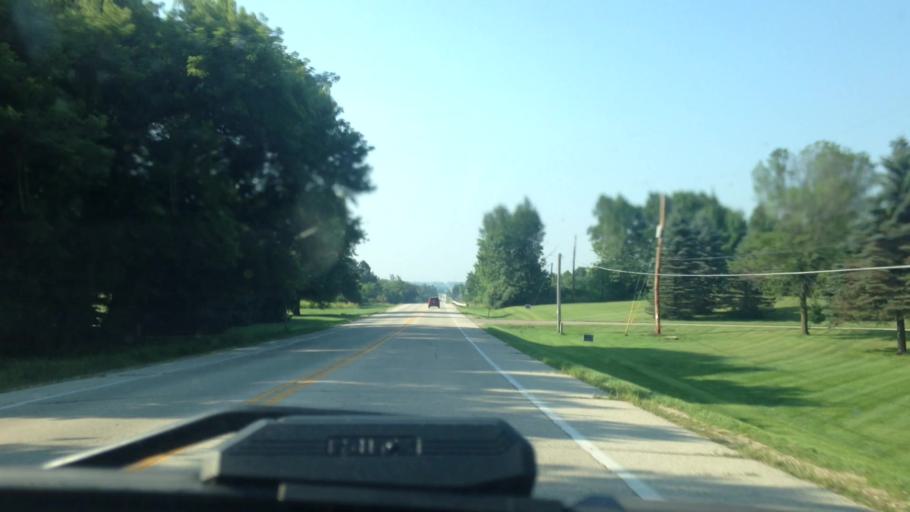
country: US
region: Wisconsin
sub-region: Washington County
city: Slinger
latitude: 43.3005
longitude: -88.2608
